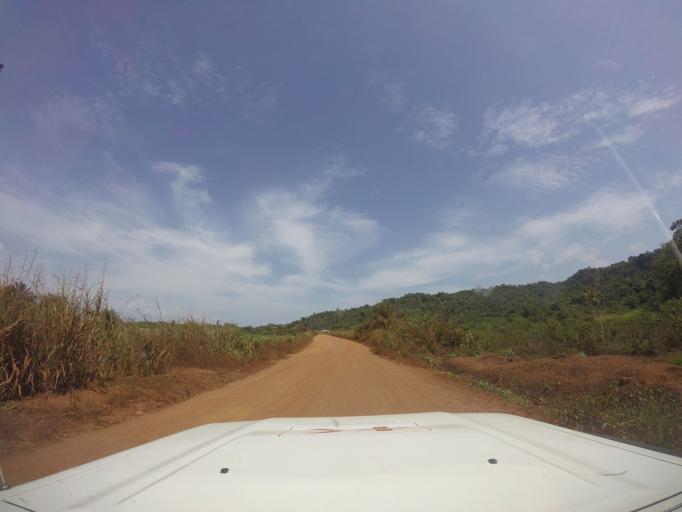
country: LR
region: Grand Cape Mount
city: Robertsport
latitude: 6.7503
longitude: -11.3613
